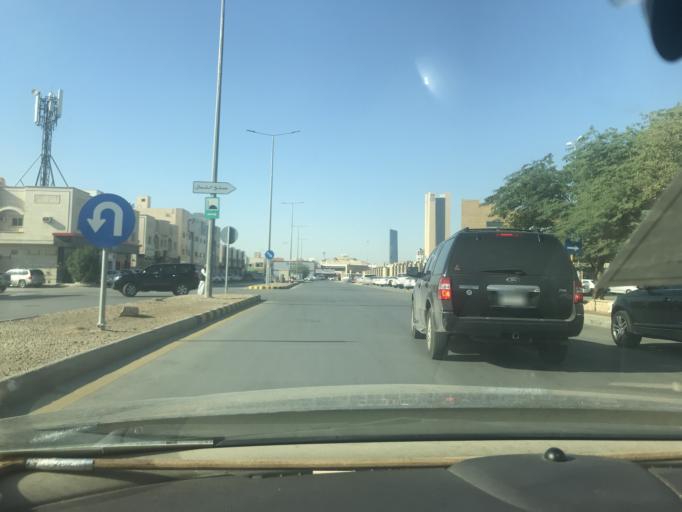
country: SA
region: Ar Riyad
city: Riyadh
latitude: 24.7528
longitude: 46.6672
